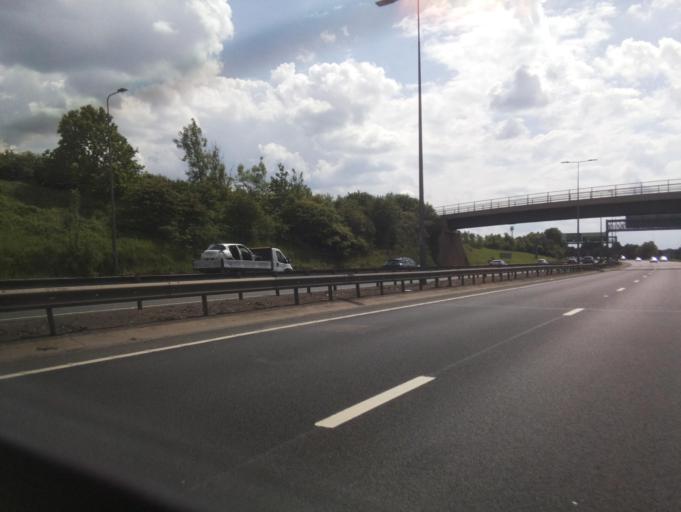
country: GB
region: England
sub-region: Redcar and Cleveland
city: Thornaby-on-Tees
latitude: 54.5444
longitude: -1.2776
